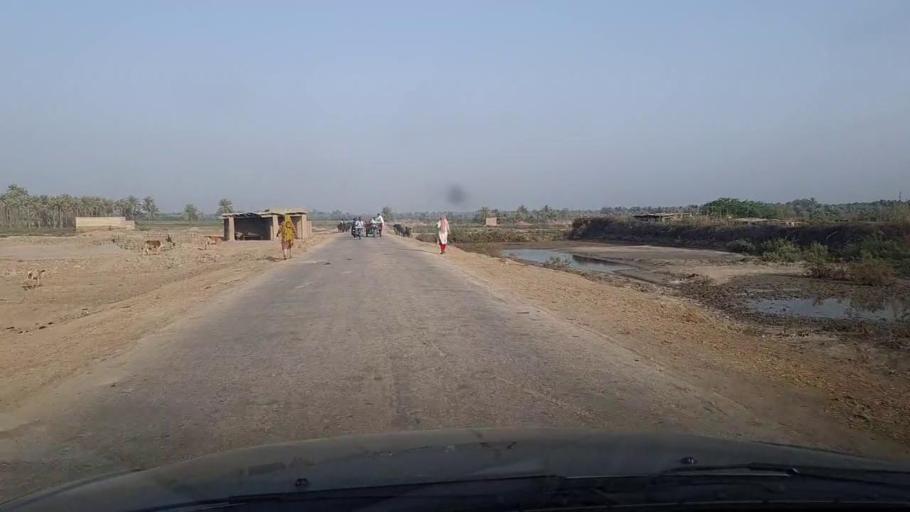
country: PK
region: Sindh
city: Khairpur
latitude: 27.5496
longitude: 68.6931
